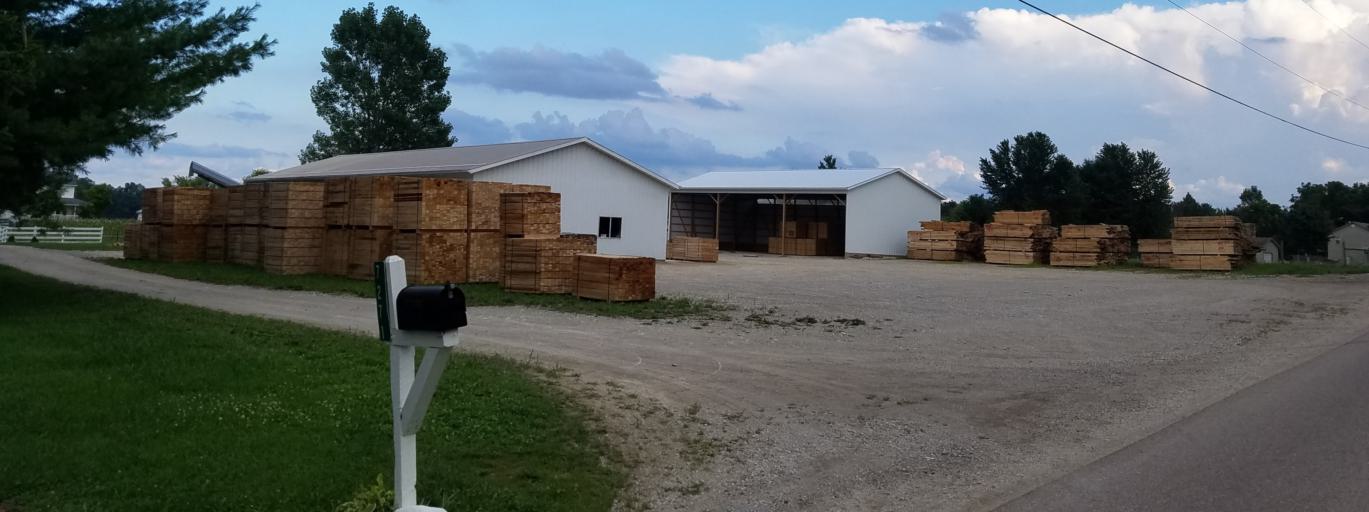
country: US
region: Ohio
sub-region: Richland County
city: Lexington
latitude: 40.6184
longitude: -82.6500
